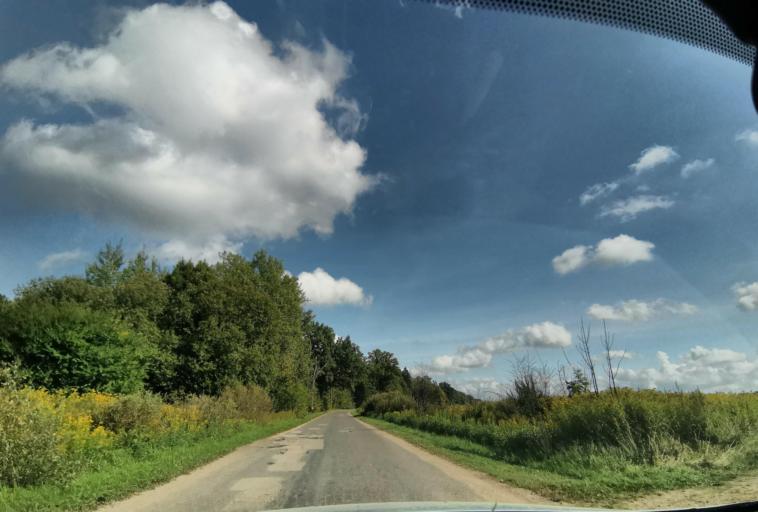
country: RU
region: Kaliningrad
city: Chernyakhovsk
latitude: 54.6652
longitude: 21.9647
